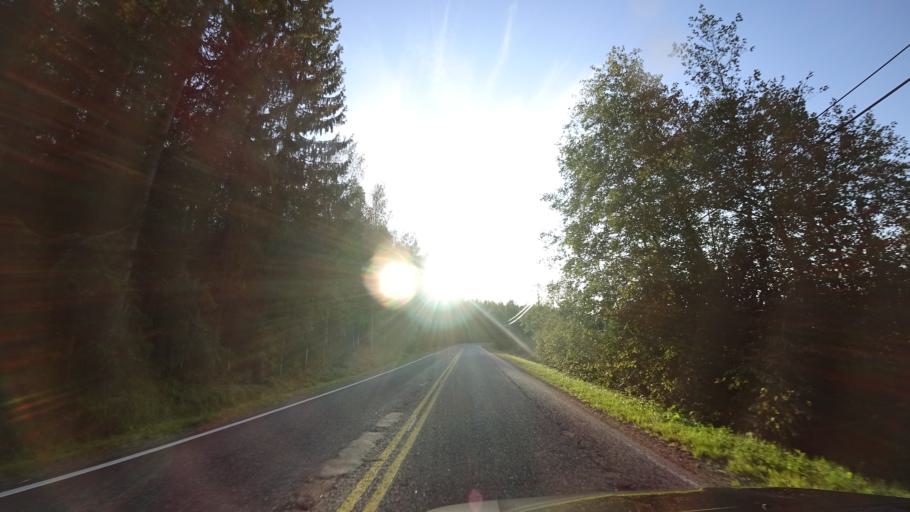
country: FI
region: Haeme
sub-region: Haemeenlinna
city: Tuulos
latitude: 61.0070
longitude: 24.8670
